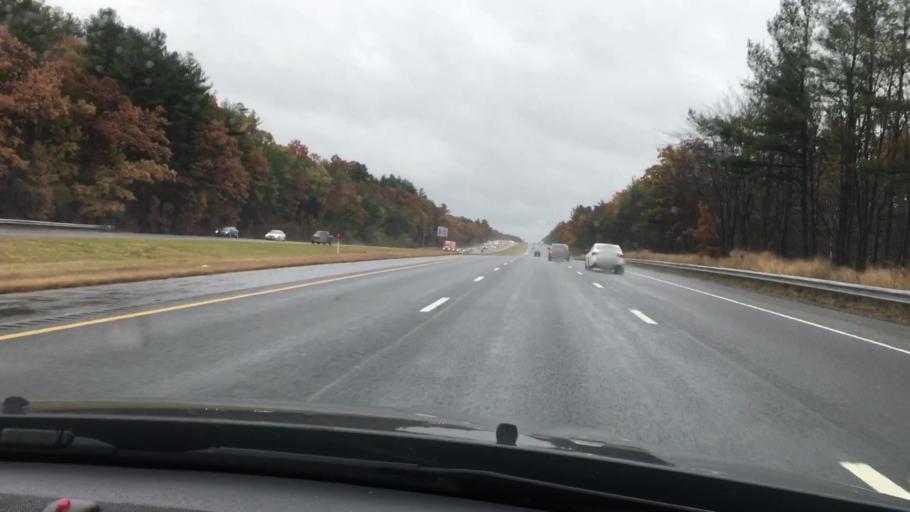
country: US
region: Massachusetts
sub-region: Middlesex County
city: Tyngsboro
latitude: 42.6666
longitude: -71.4350
